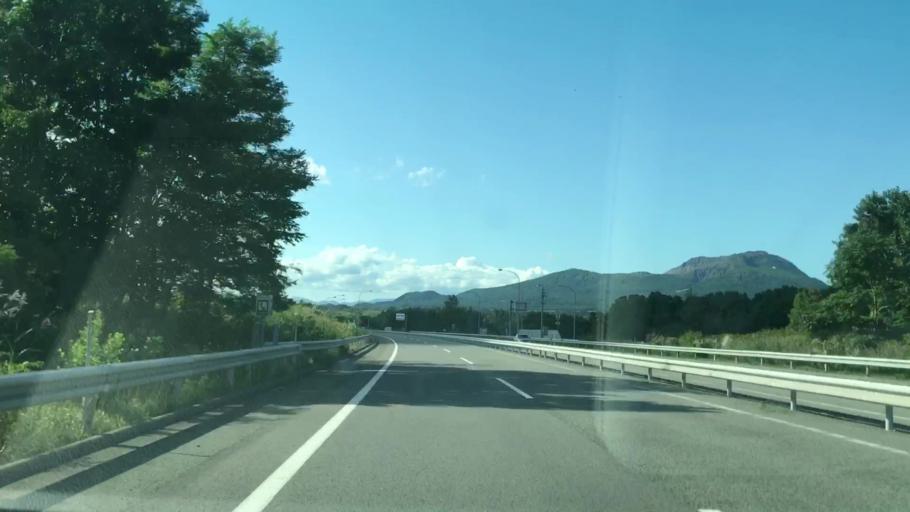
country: JP
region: Hokkaido
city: Date
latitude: 42.4846
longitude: 140.8929
